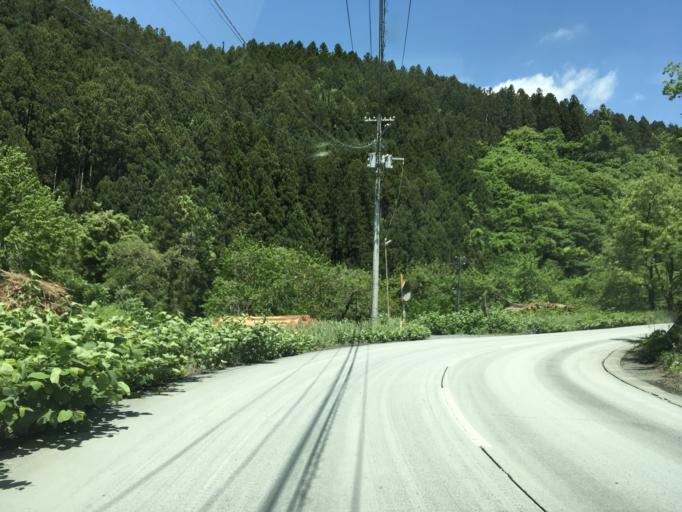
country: JP
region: Miyagi
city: Wakuya
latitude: 38.6593
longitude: 141.3219
